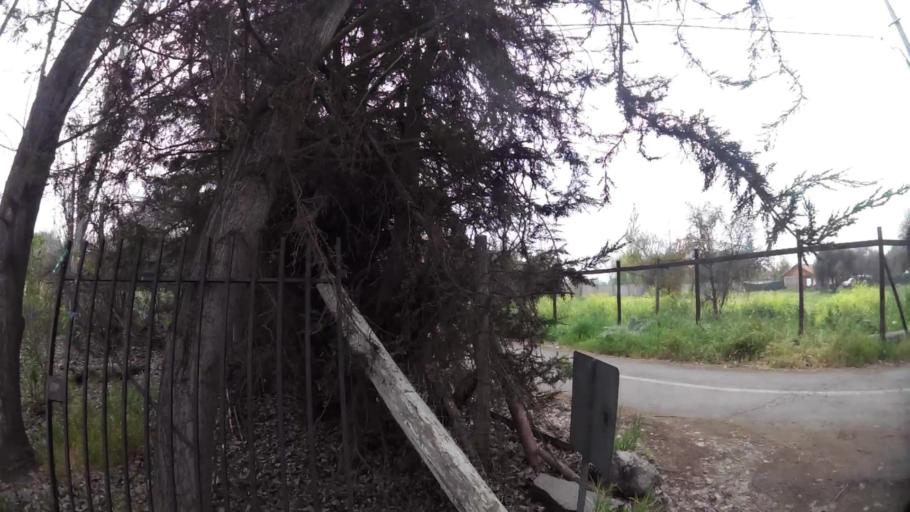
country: CL
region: Santiago Metropolitan
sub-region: Provincia de Chacabuco
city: Lampa
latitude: -33.2421
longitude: -70.7916
